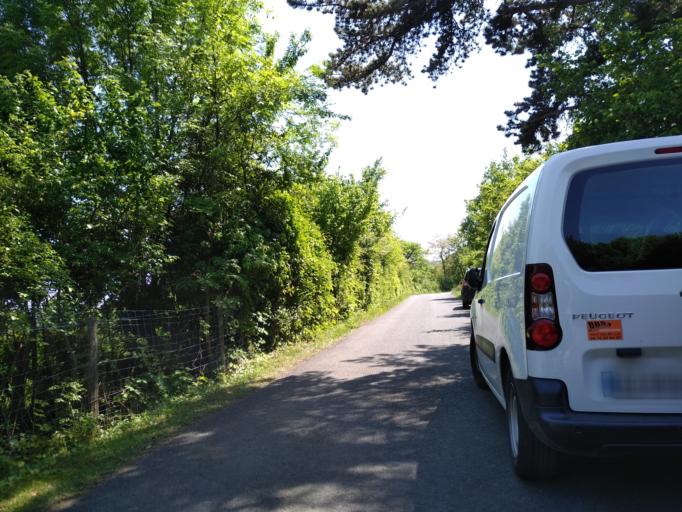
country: FR
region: Rhone-Alpes
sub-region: Departement du Rhone
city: Fontaines-sur-Saone
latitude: 45.8362
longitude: 4.8154
